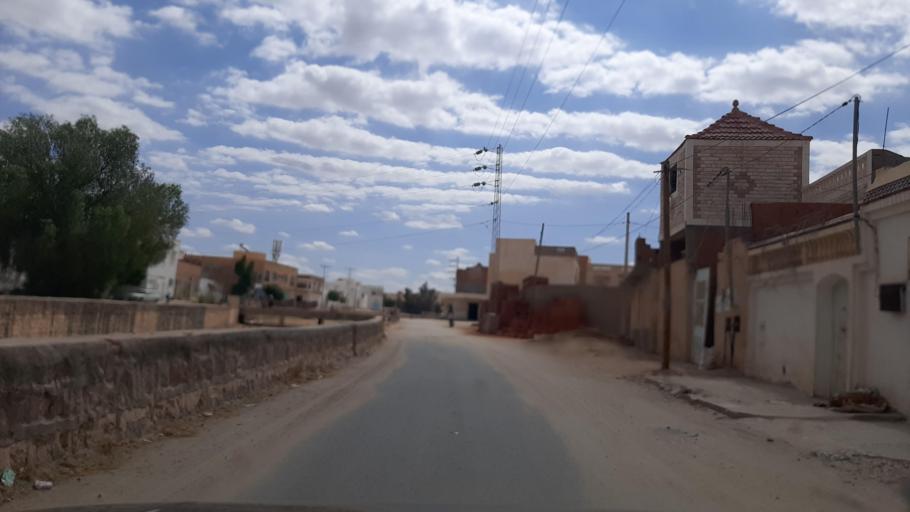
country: TN
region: Tataouine
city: Tataouine
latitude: 32.9303
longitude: 10.4563
